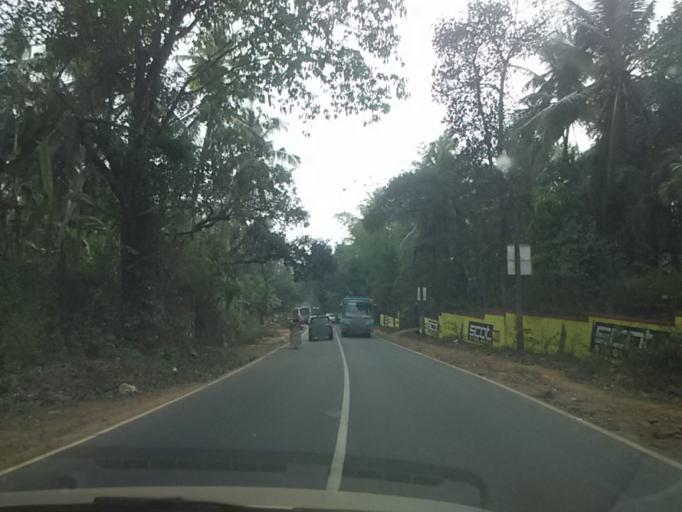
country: IN
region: Kerala
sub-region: Kozhikode
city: Naduvannur
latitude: 11.5308
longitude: 75.7718
